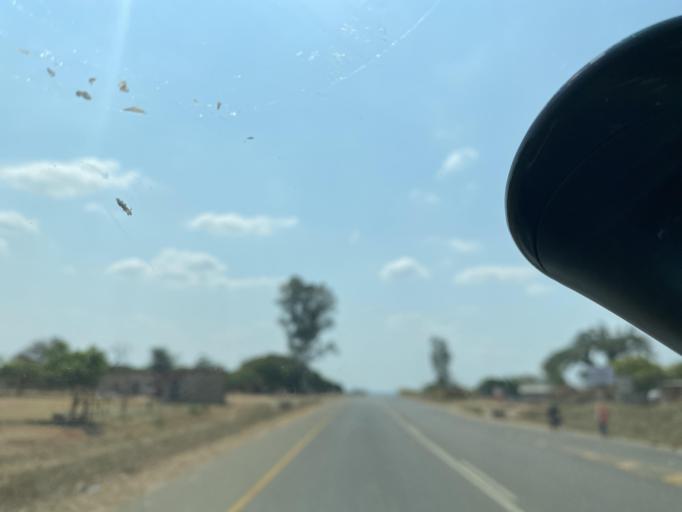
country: ZM
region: Lusaka
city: Chongwe
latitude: -15.5775
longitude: 28.7026
